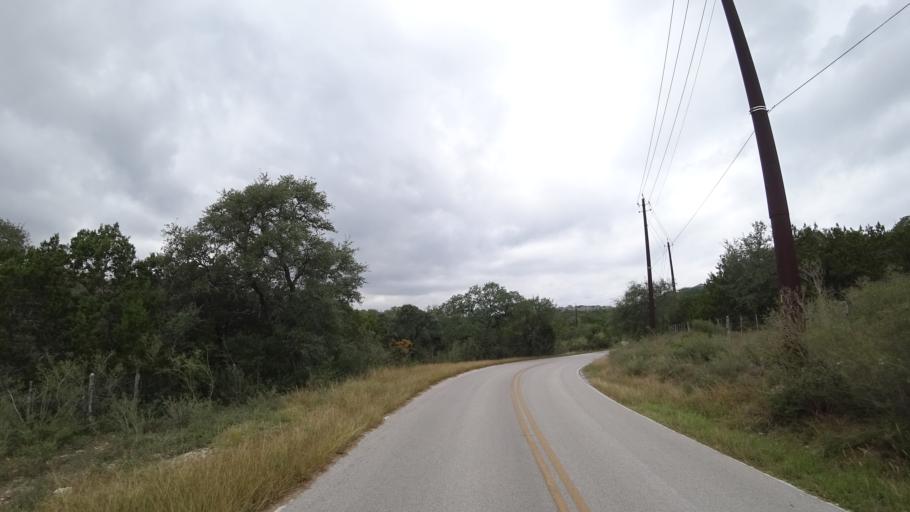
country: US
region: Texas
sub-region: Travis County
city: Bee Cave
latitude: 30.3368
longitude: -97.9098
